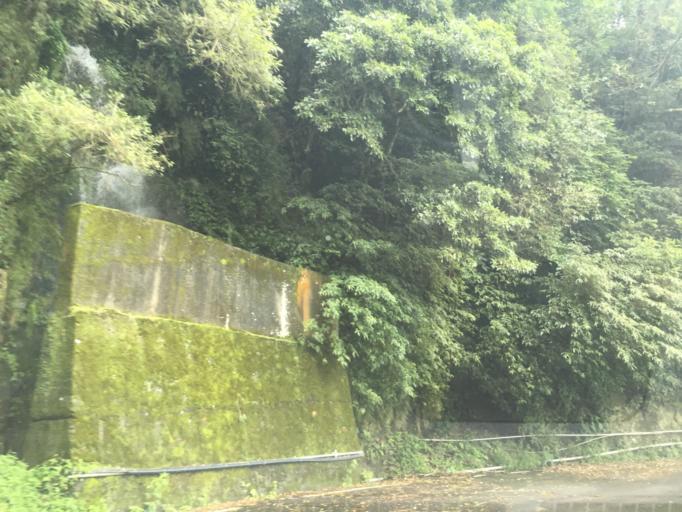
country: TW
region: Taiwan
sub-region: Yunlin
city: Douliu
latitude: 23.5595
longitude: 120.6628
